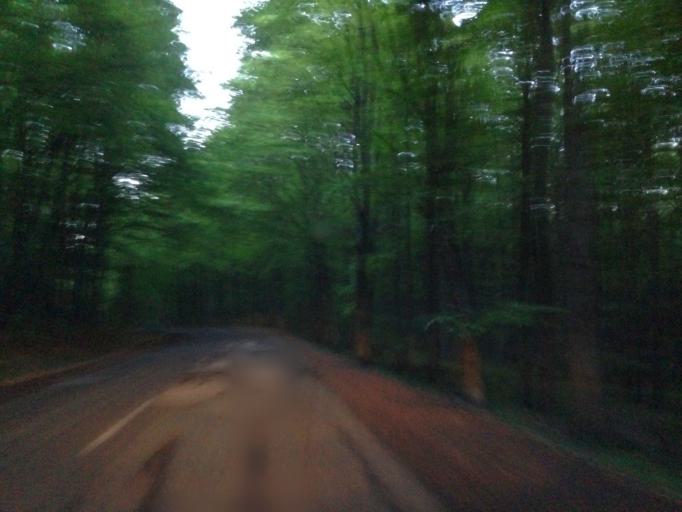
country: HU
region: Heves
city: Gyongyostarjan
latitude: 47.8948
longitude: 19.8759
